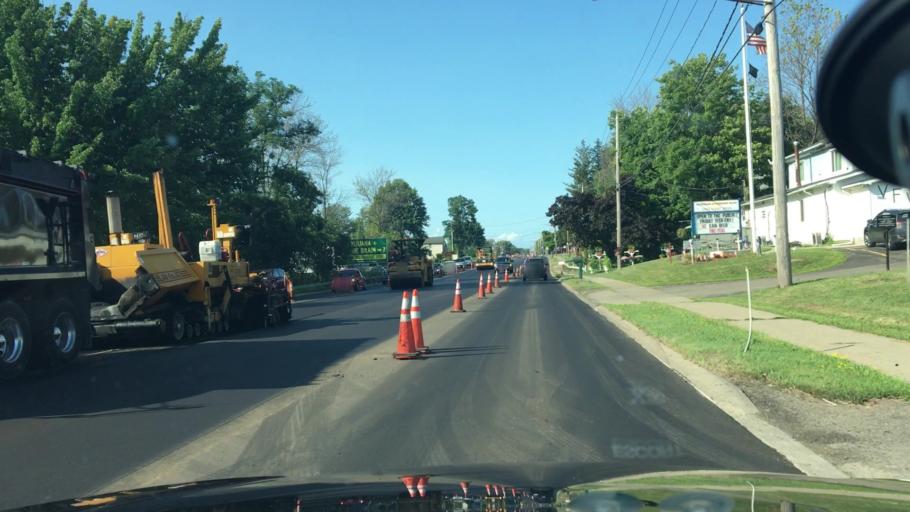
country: US
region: New York
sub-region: Erie County
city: Angola on the Lake
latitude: 42.6401
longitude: -79.0470
